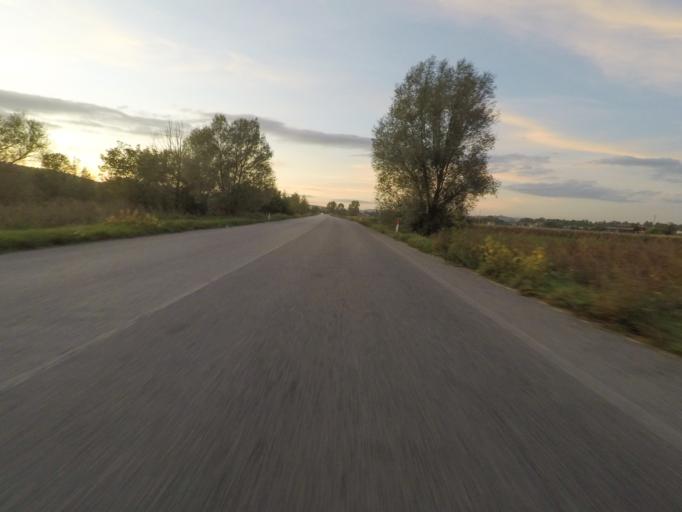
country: IT
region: Tuscany
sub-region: Provincia di Siena
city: Sinalunga
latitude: 43.2152
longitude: 11.7613
